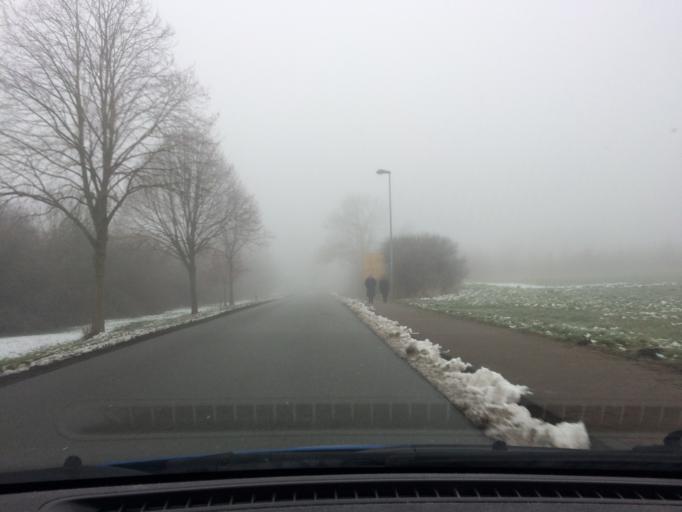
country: DE
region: Schleswig-Holstein
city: Lauenburg
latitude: 53.3832
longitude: 10.5418
